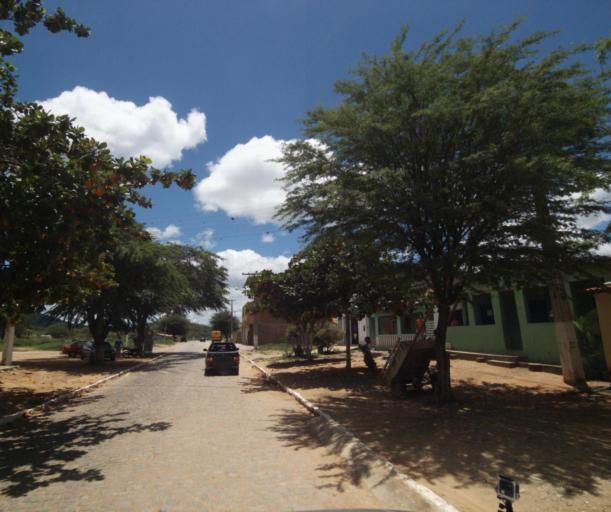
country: BR
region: Bahia
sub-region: Pocoes
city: Pocoes
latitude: -14.3773
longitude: -40.5069
